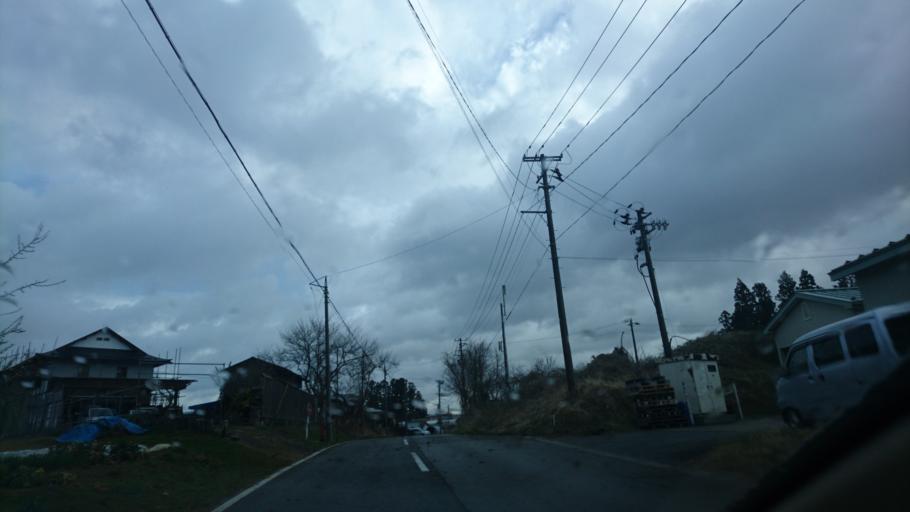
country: JP
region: Iwate
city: Ichinoseki
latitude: 38.7634
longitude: 141.0321
